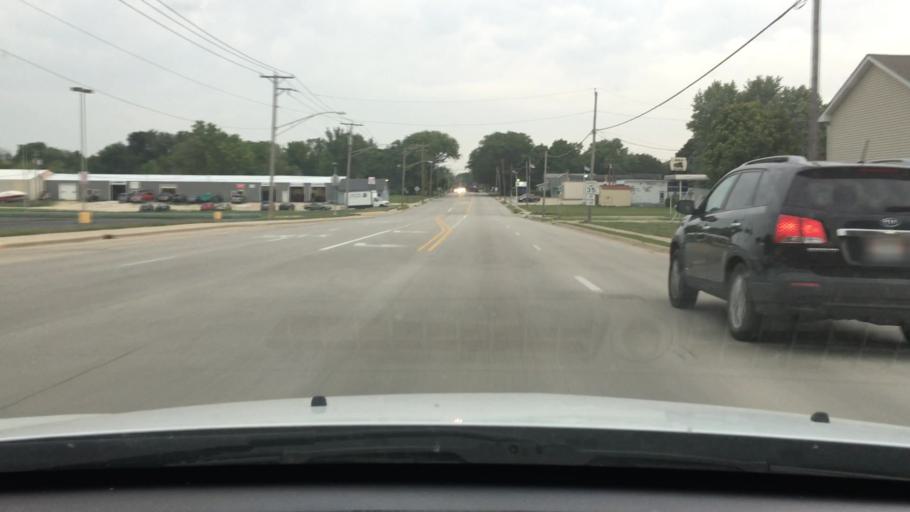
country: US
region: Illinois
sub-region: DeKalb County
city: DeKalb
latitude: 41.9132
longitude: -88.7535
